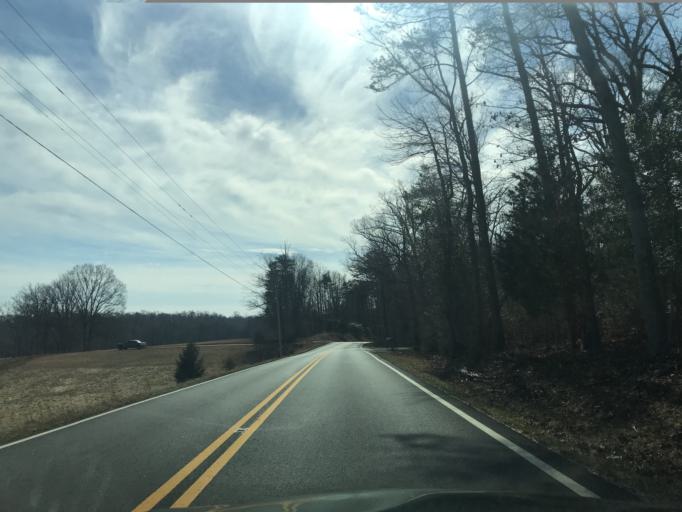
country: US
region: Maryland
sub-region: Charles County
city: Indian Head
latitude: 38.5170
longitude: -77.1458
